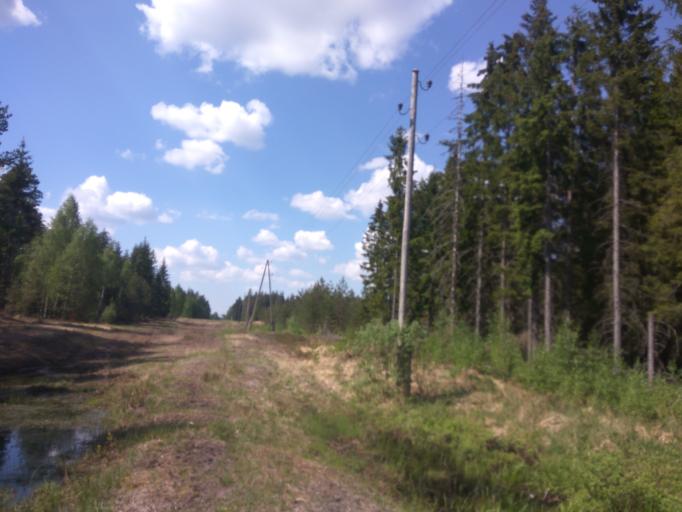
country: LV
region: Kuldigas Rajons
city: Kuldiga
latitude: 57.1839
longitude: 21.9961
